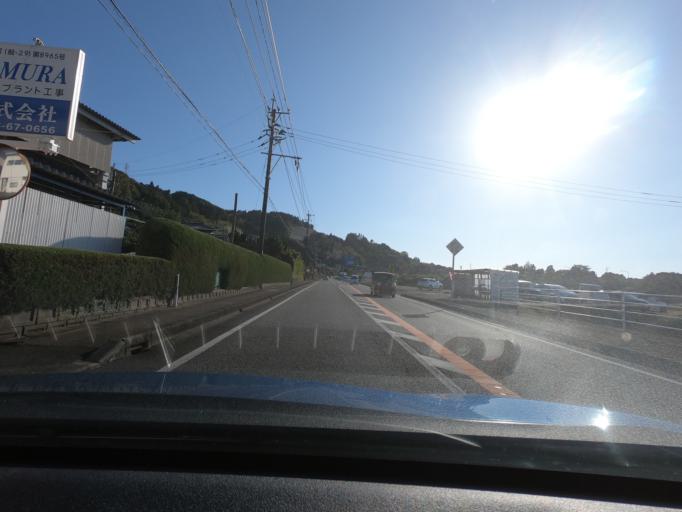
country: JP
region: Kagoshima
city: Izumi
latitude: 32.1522
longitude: 130.3644
